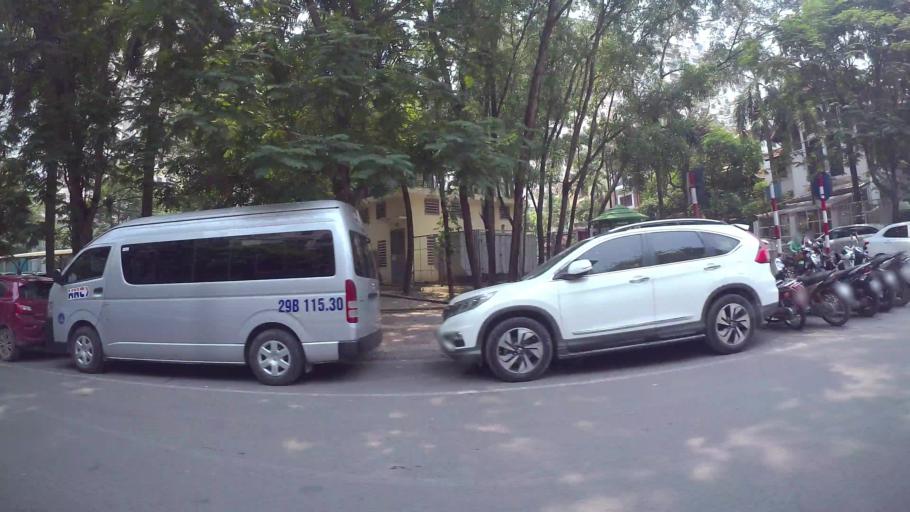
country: VN
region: Ha Noi
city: Thanh Xuan
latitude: 21.0072
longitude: 105.8056
